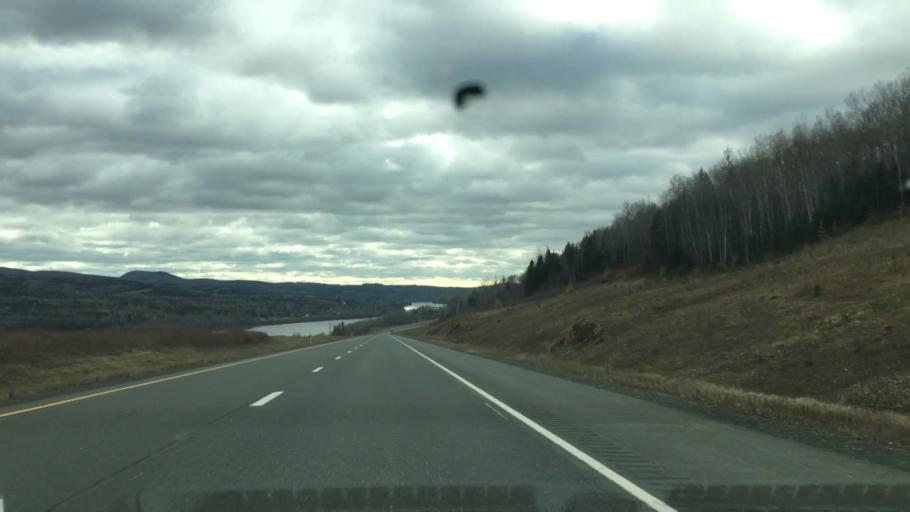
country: US
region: Maine
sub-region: Aroostook County
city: Fort Fairfield
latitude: 46.6884
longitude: -67.7366
